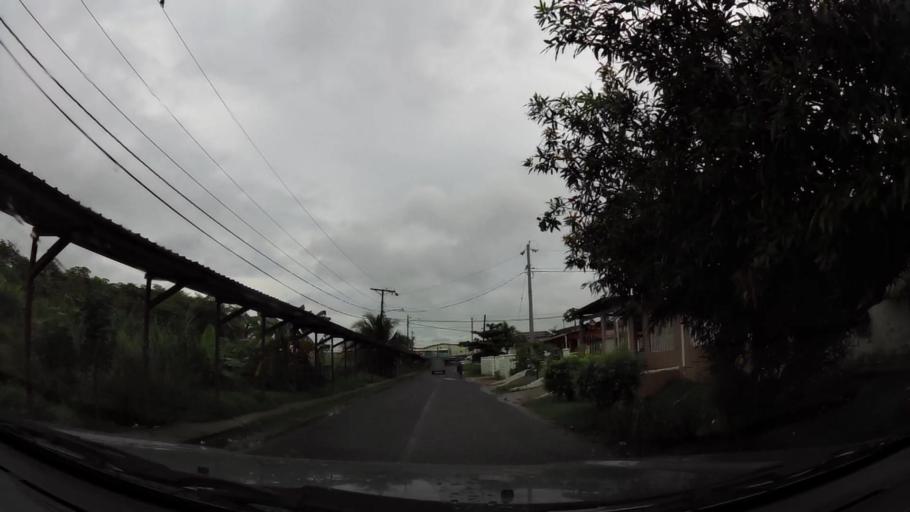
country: PA
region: Colon
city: Arco Iris
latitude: 9.3359
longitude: -79.8790
